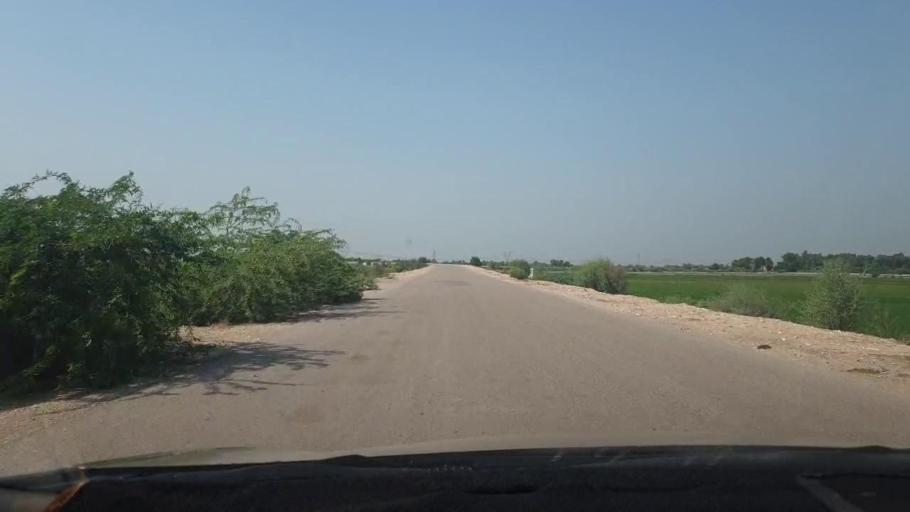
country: PK
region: Sindh
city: Larkana
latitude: 27.6017
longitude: 68.2431
